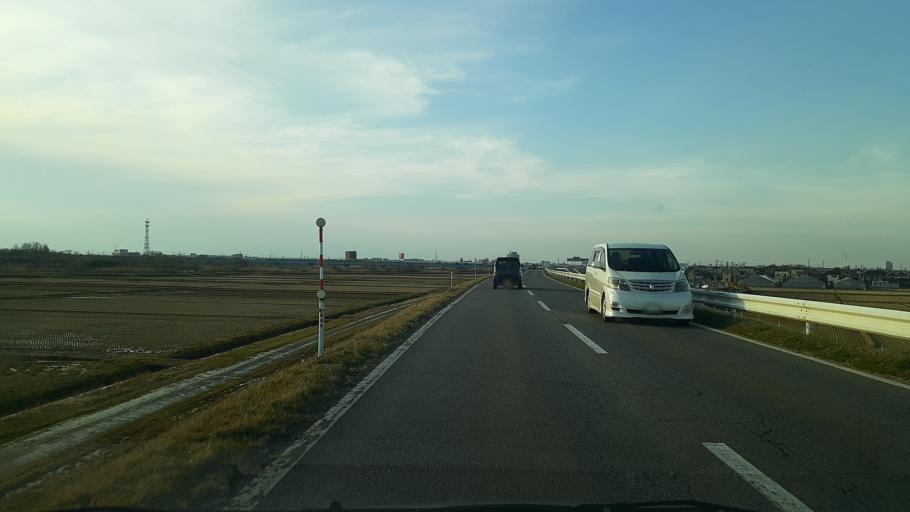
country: JP
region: Niigata
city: Niigata-shi
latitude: 37.8498
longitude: 139.0274
